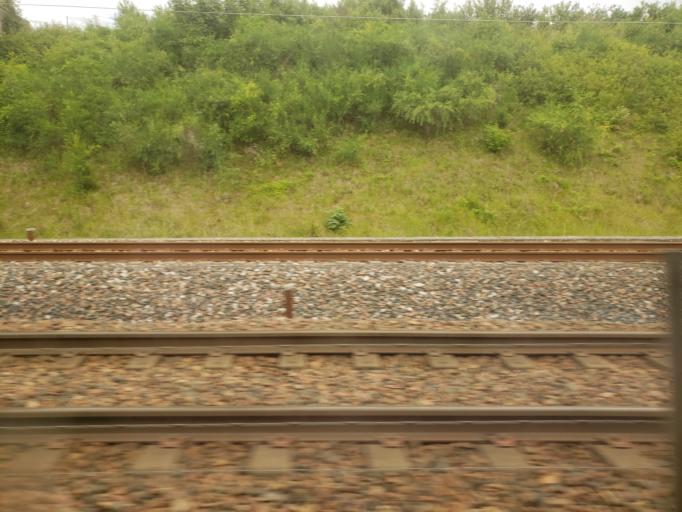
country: FR
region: Ile-de-France
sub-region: Departement de Seine-et-Marne
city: Serris
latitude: 48.8641
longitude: 2.7819
